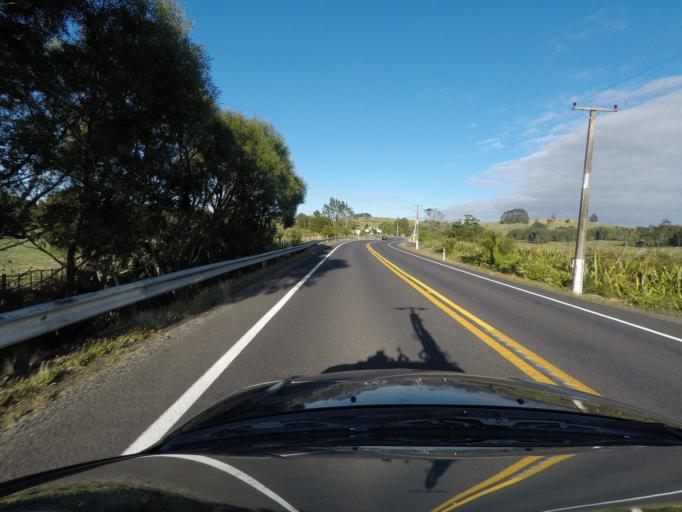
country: NZ
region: Northland
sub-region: Far North District
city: Kawakawa
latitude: -35.4952
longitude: 174.1544
